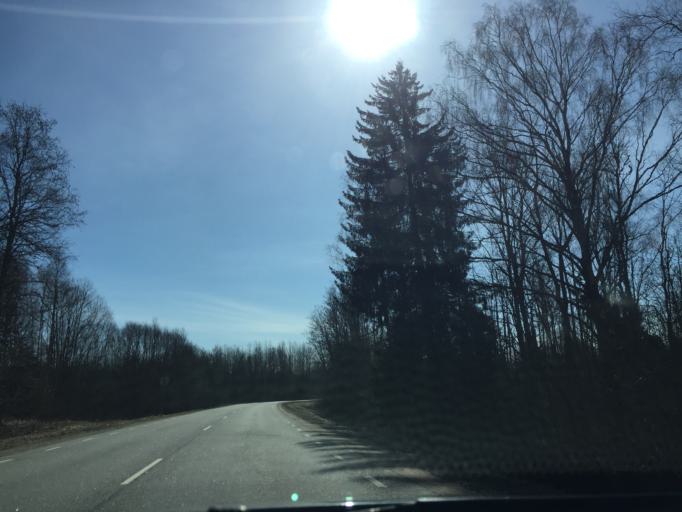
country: EE
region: Laeaene
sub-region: Lihula vald
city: Lihula
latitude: 58.6261
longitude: 23.6869
